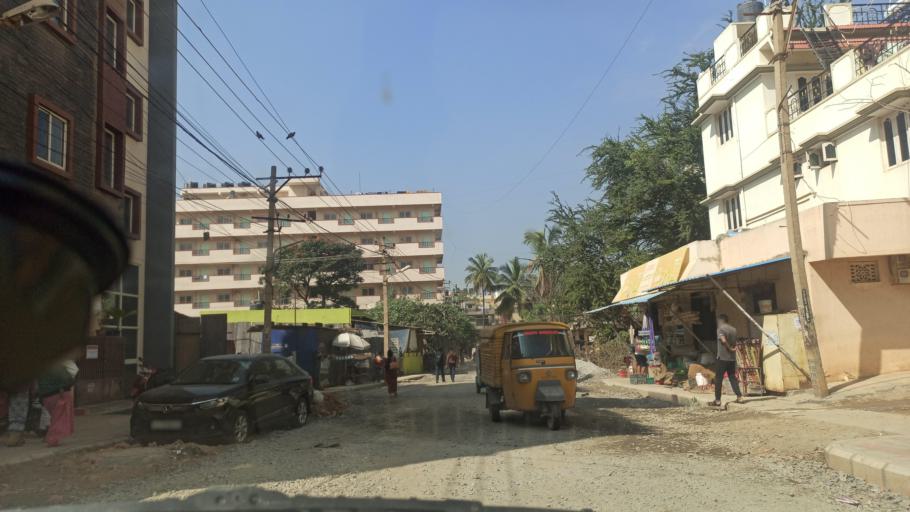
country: IN
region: Karnataka
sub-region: Bangalore Urban
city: Bangalore
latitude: 12.9281
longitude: 77.6877
